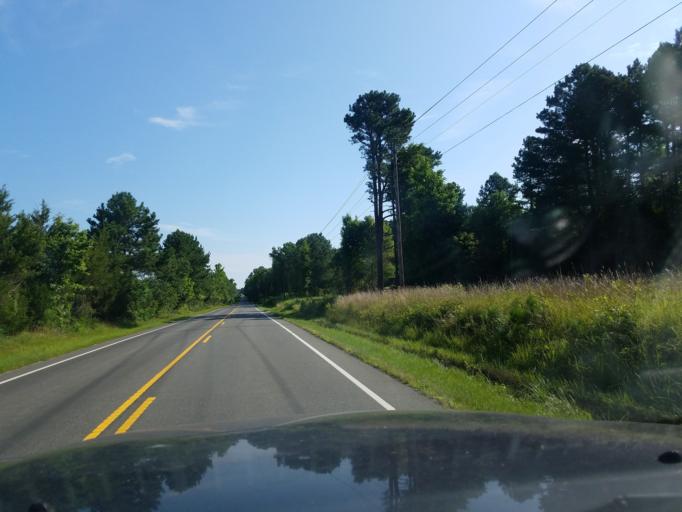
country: US
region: North Carolina
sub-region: Granville County
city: Butner
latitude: 36.2156
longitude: -78.7242
